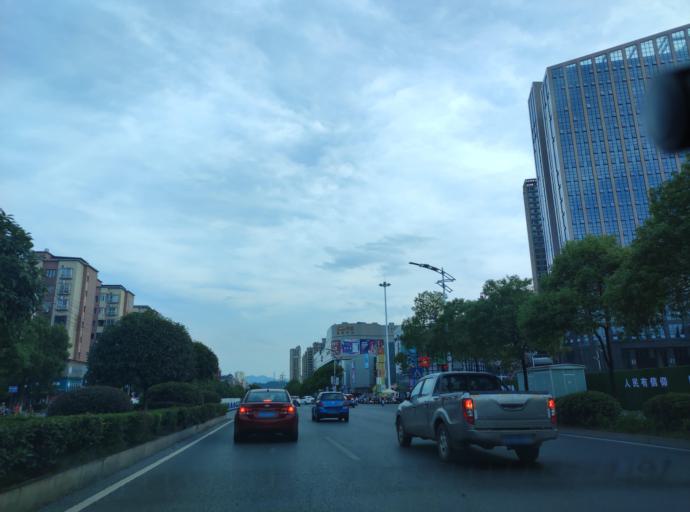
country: CN
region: Jiangxi Sheng
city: Pingxiang
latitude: 27.6381
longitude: 113.8702
